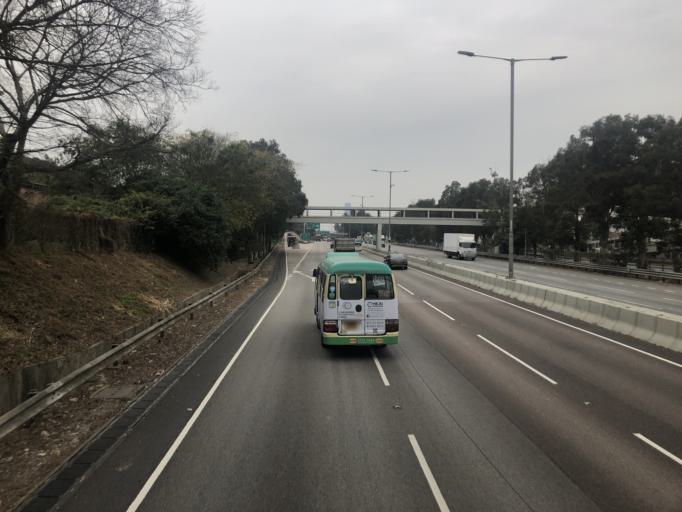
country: CN
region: Guangdong
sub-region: Shenzhen
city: Shenzhen
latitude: 22.5038
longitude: 114.0957
